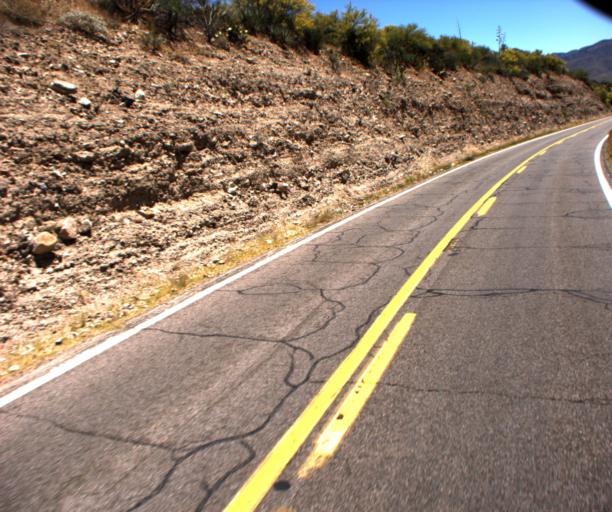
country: US
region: Arizona
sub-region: Pinal County
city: Kearny
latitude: 33.1674
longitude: -110.8055
